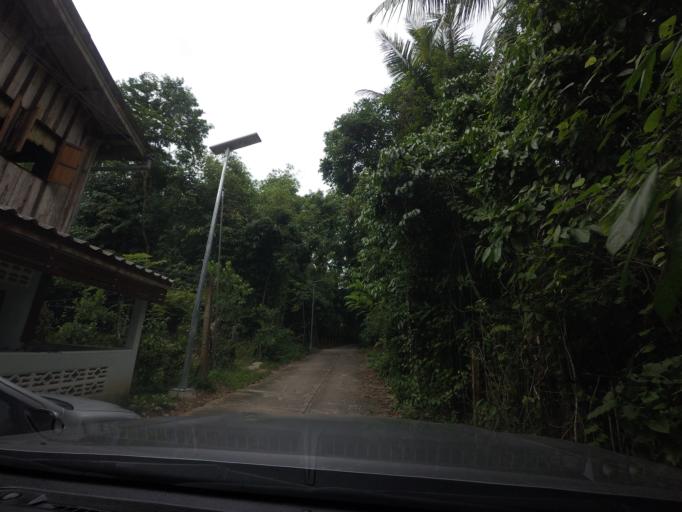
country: TH
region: Narathiwat
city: Rueso
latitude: 6.3839
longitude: 101.5181
